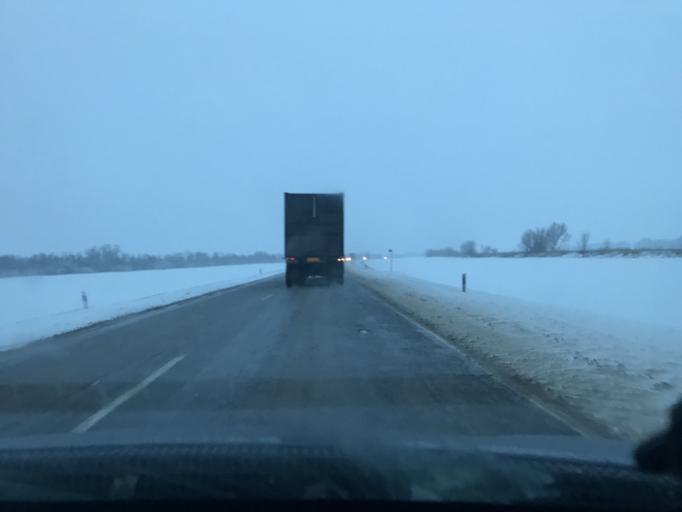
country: RU
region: Rostov
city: Letnik
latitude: 46.0580
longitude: 41.2095
